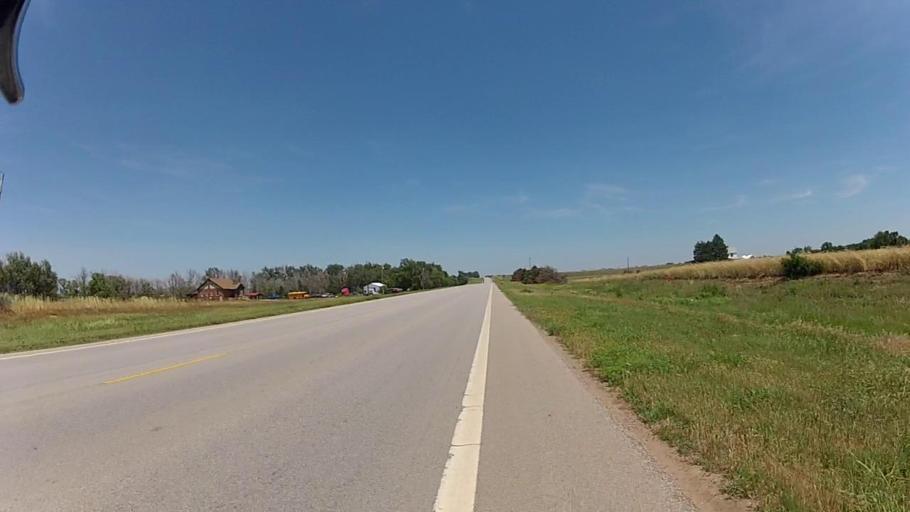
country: US
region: Kansas
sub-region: Harper County
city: Harper
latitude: 37.2386
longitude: -98.1224
